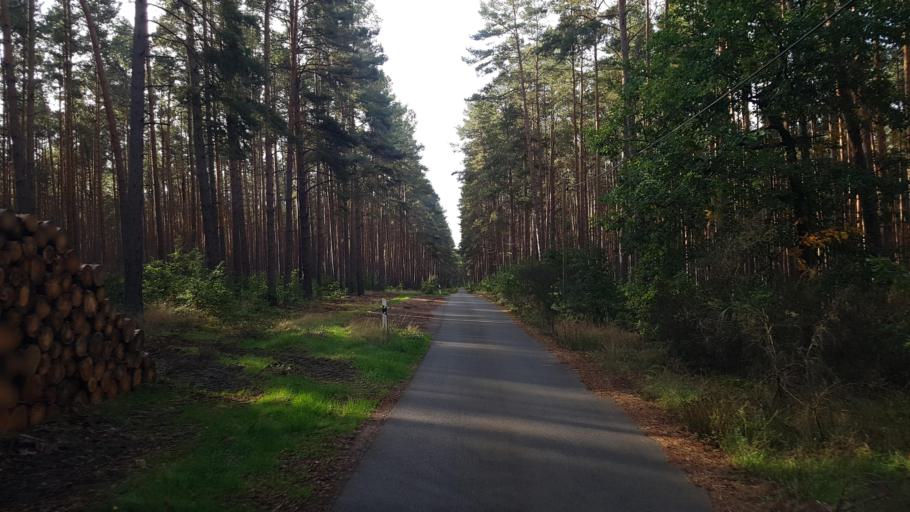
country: DE
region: Brandenburg
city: Hohenbucko
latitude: 51.8286
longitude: 13.5319
